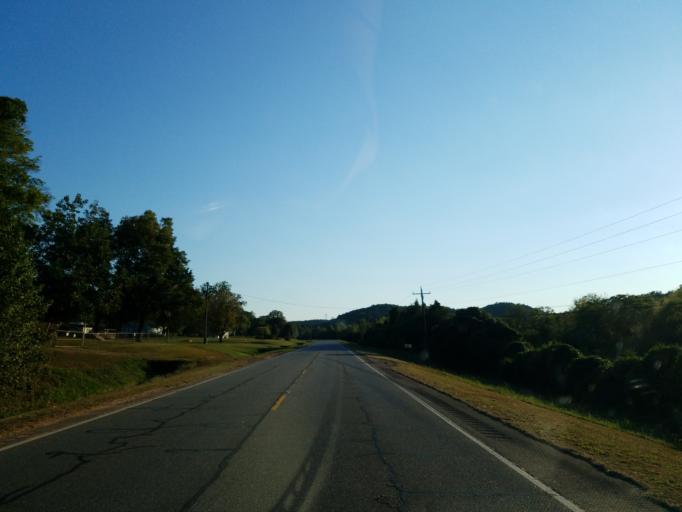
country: US
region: Georgia
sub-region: Bartow County
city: Rydal
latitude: 34.4059
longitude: -84.7050
